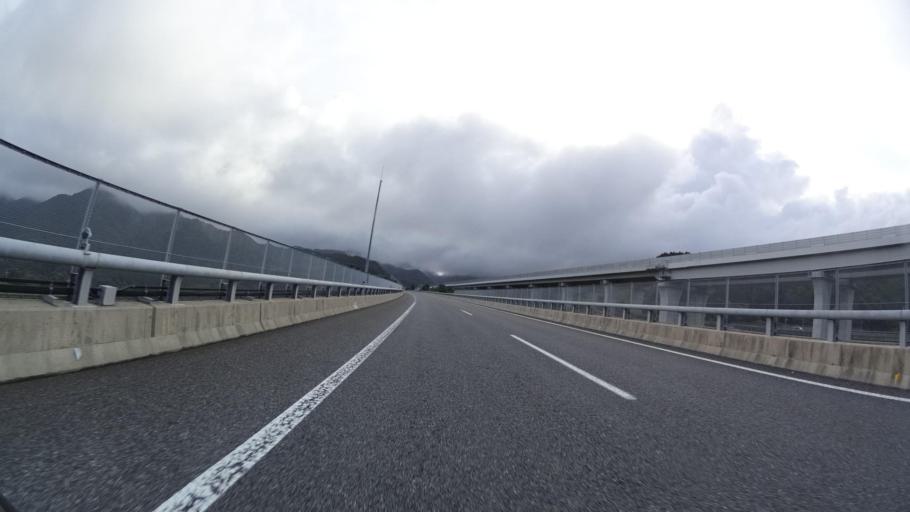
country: JP
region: Mie
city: Kameyama
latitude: 34.9189
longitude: 136.4134
